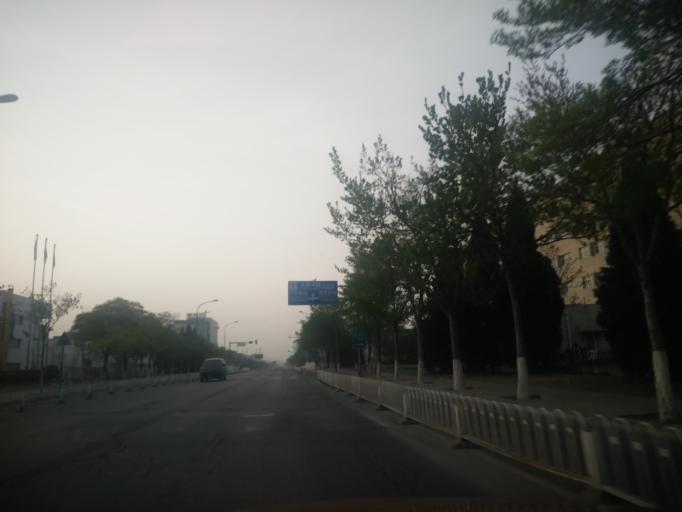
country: CN
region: Beijing
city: Jiugong
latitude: 39.7963
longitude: 116.5098
